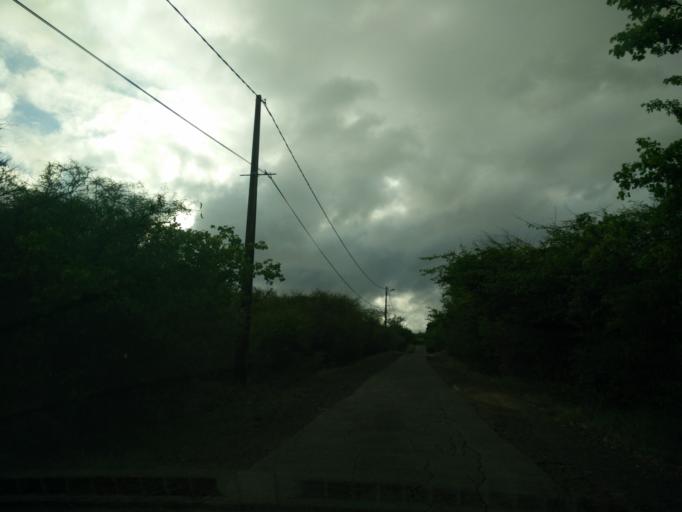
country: MQ
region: Martinique
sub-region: Martinique
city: Le Marin
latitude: 14.4367
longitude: -60.8311
